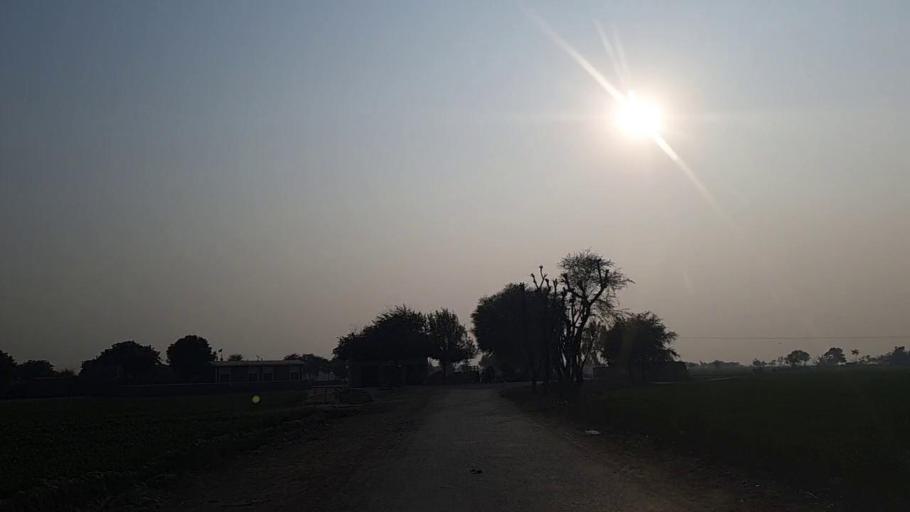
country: PK
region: Sindh
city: Nawabshah
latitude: 26.2258
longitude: 68.4806
